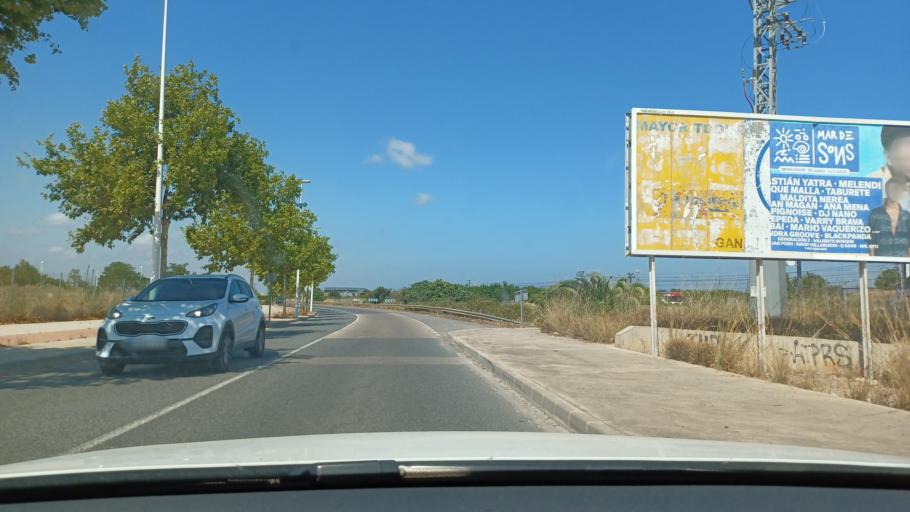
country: ES
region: Valencia
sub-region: Provincia de Valencia
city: Sagunto
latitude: 39.6863
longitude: -0.2645
